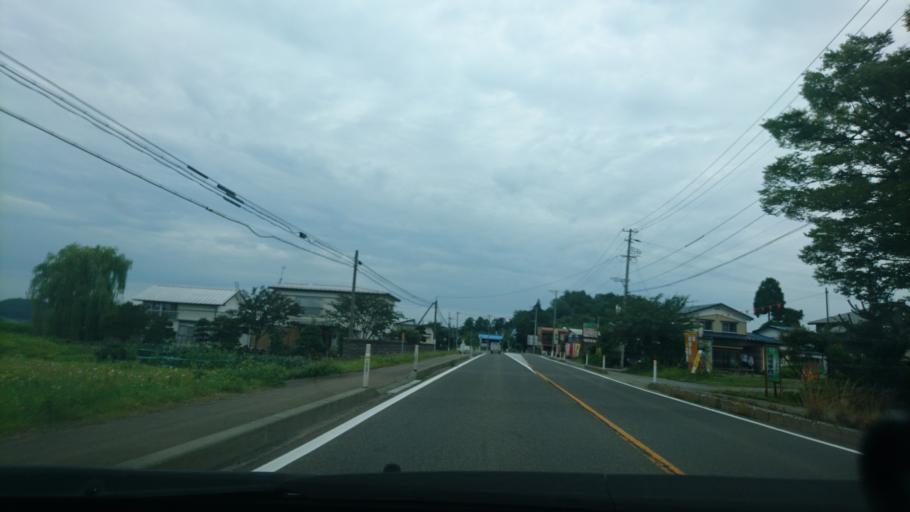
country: JP
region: Akita
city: Yokotemachi
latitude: 39.3517
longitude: 140.5625
